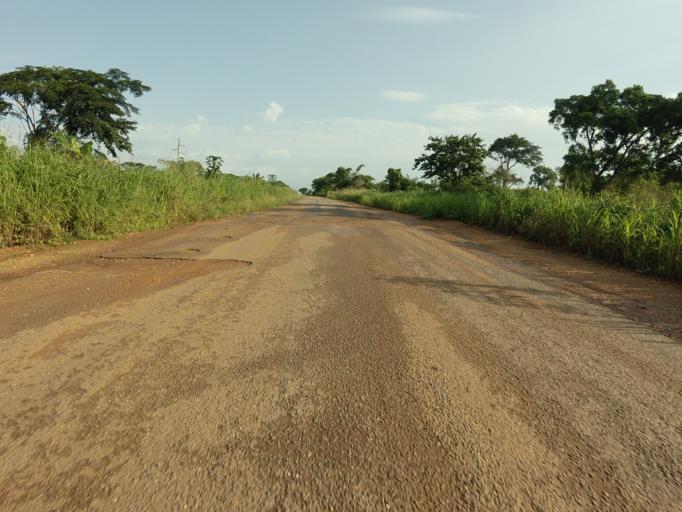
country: GH
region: Volta
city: Hohoe
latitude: 7.0917
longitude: 0.4454
